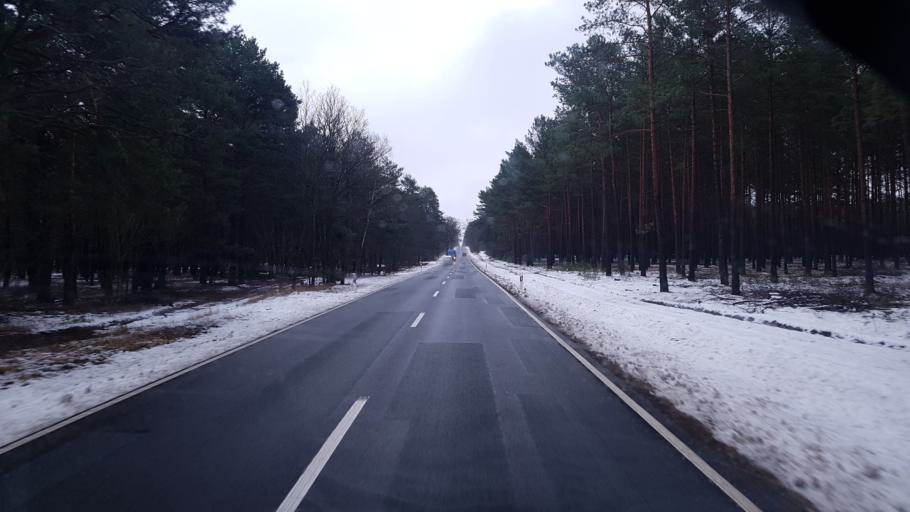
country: DE
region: Brandenburg
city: Jamlitz
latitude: 51.9833
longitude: 14.4343
